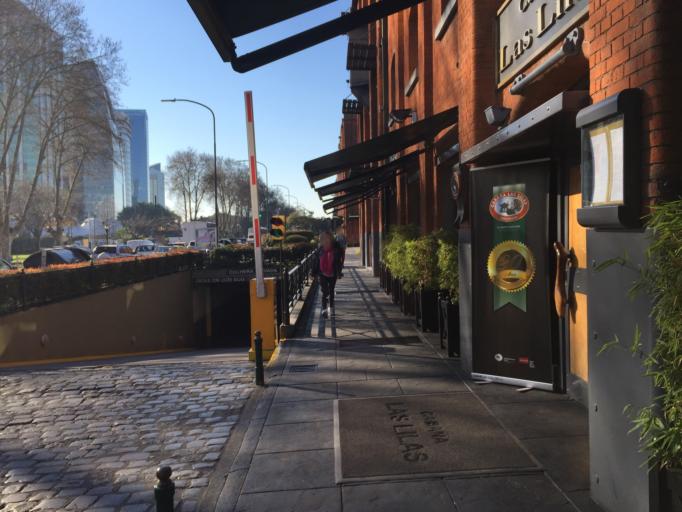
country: AR
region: Buenos Aires F.D.
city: Buenos Aires
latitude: -34.6039
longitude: -58.3670
